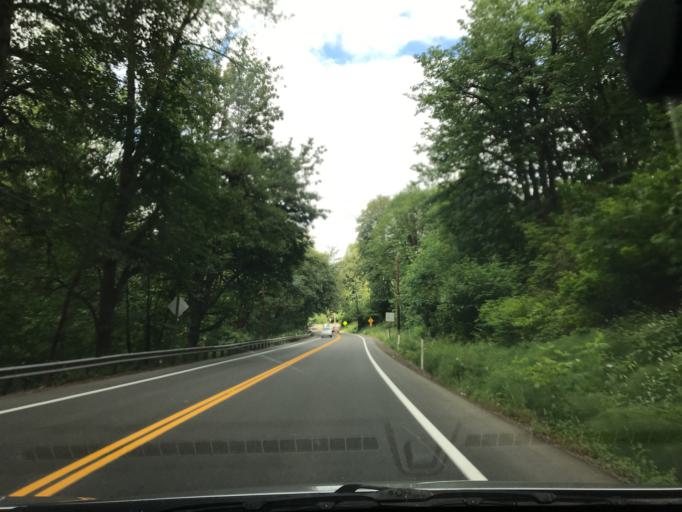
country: US
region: Washington
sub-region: King County
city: Lea Hill
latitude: 47.3161
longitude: -122.1448
